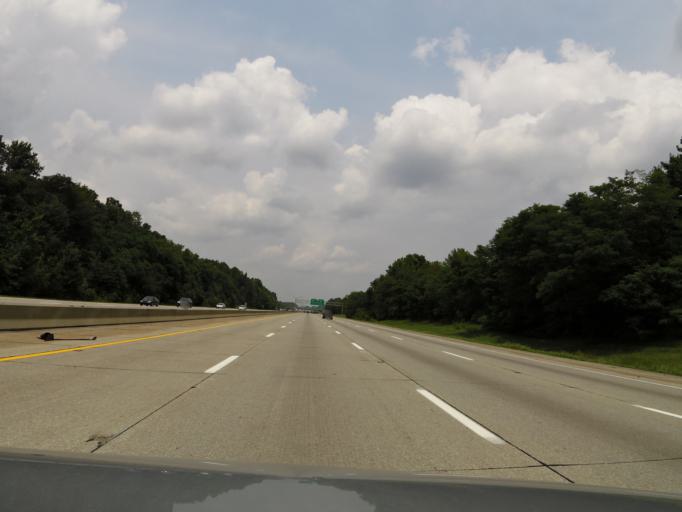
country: US
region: Kentucky
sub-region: Jefferson County
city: Heritage Creek
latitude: 38.1026
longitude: -85.7009
